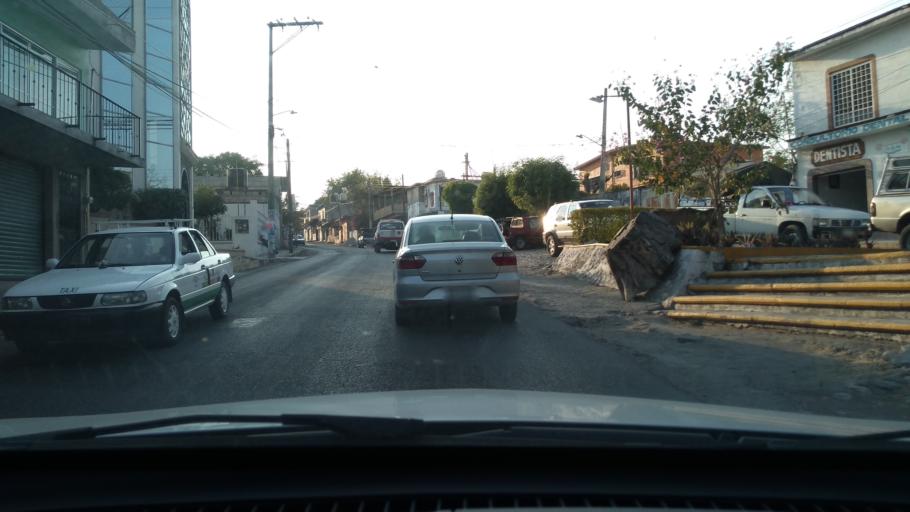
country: MX
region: Morelos
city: Puente de Ixtla
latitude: 18.6223
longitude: -99.3196
